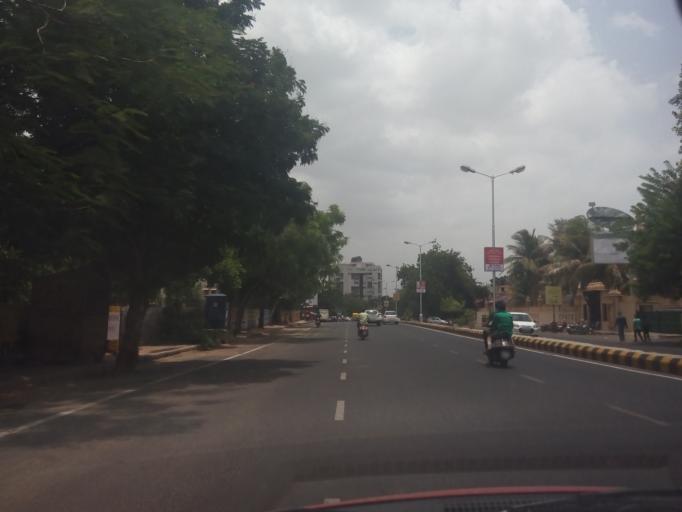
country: IN
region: Gujarat
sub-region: Ahmadabad
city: Sarkhej
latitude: 23.0432
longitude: 72.5222
